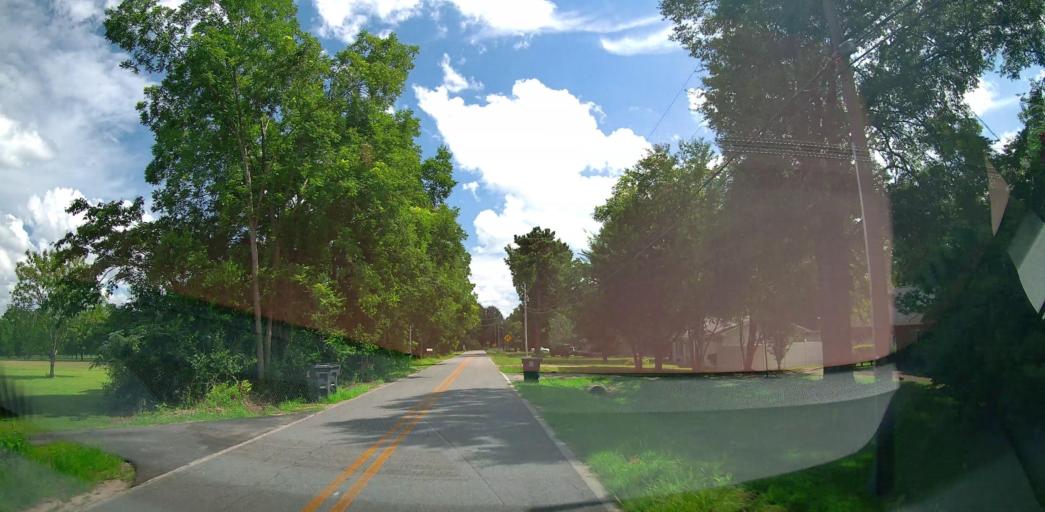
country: US
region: Georgia
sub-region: Houston County
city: Centerville
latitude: 32.7060
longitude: -83.6792
